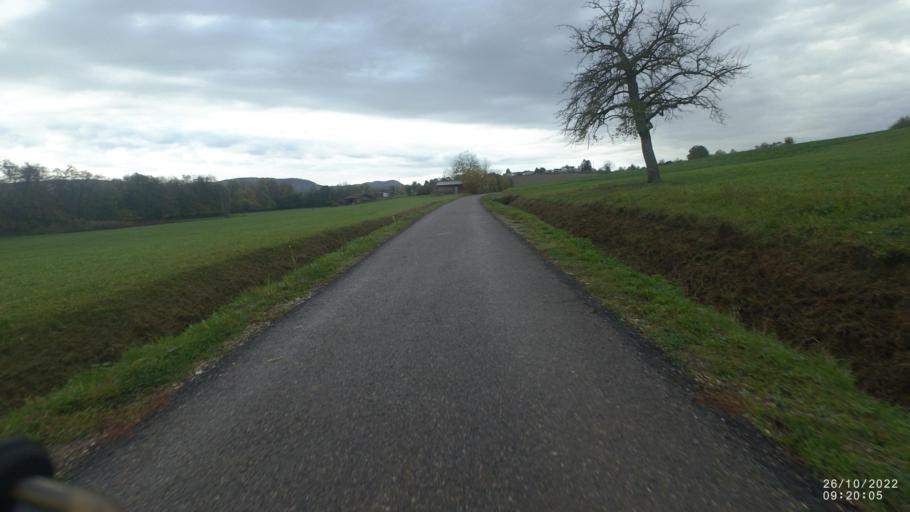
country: DE
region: Baden-Wuerttemberg
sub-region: Regierungsbezirk Stuttgart
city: Heiningen
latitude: 48.6695
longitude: 9.6589
